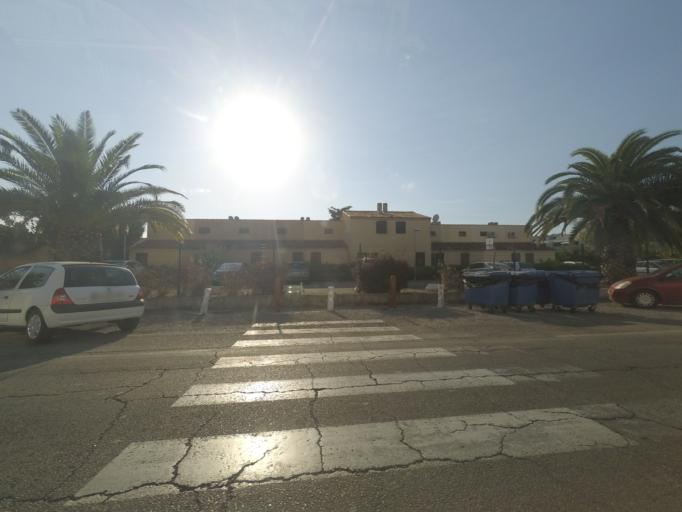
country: FR
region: Languedoc-Roussillon
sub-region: Departement du Gard
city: Le Grau-du-Roi
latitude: 43.5276
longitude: 4.1494
